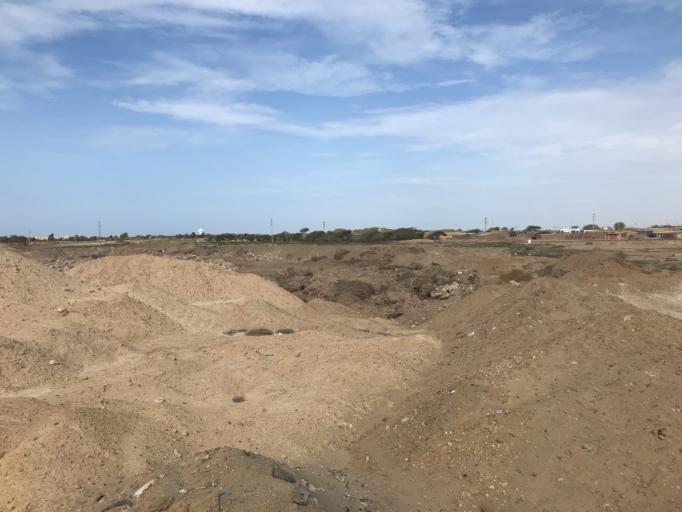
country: PE
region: Lambayeque
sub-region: Provincia de Chiclayo
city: Eten
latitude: -6.9006
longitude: -79.8423
